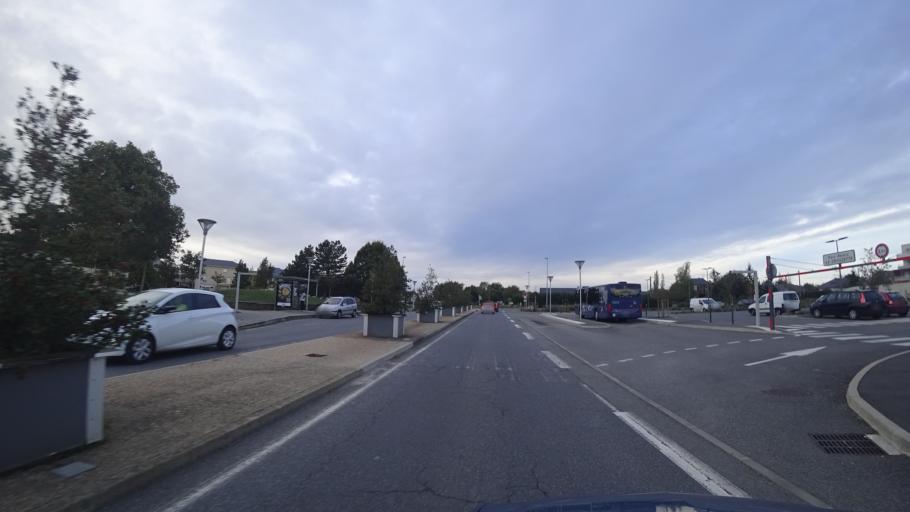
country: FR
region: Midi-Pyrenees
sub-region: Departement de l'Aveyron
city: Olemps
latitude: 44.3376
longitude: 2.5552
